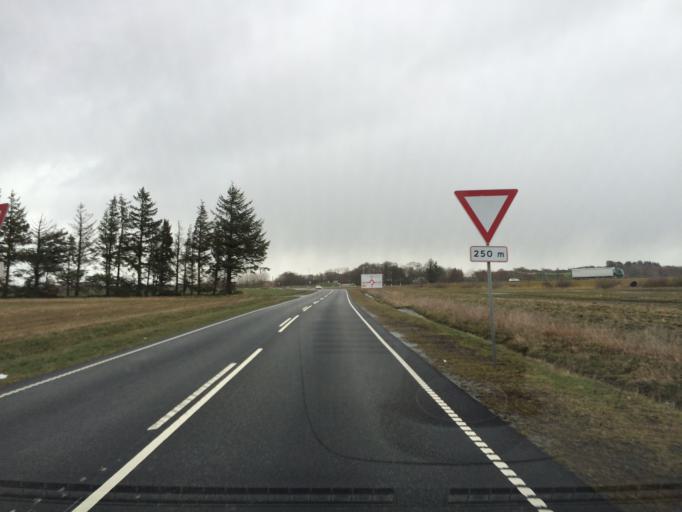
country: DK
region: Central Jutland
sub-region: Herning Kommune
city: Vildbjerg
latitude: 56.1829
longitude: 8.6972
